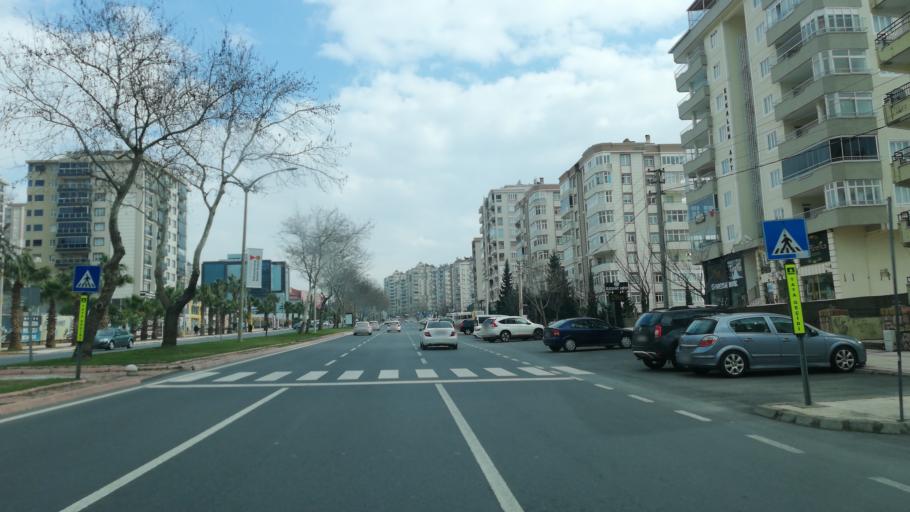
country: TR
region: Kahramanmaras
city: Kahramanmaras
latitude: 37.5900
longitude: 36.8738
